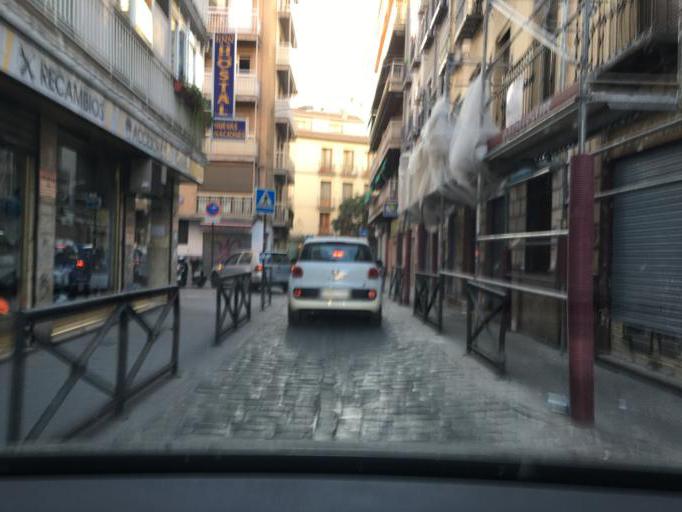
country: ES
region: Andalusia
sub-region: Provincia de Granada
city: Granada
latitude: 37.1817
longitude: -3.6020
